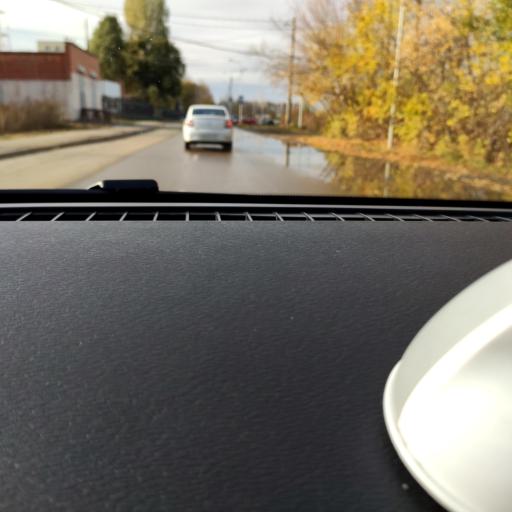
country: RU
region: Samara
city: Samara
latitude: 53.2057
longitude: 50.1687
